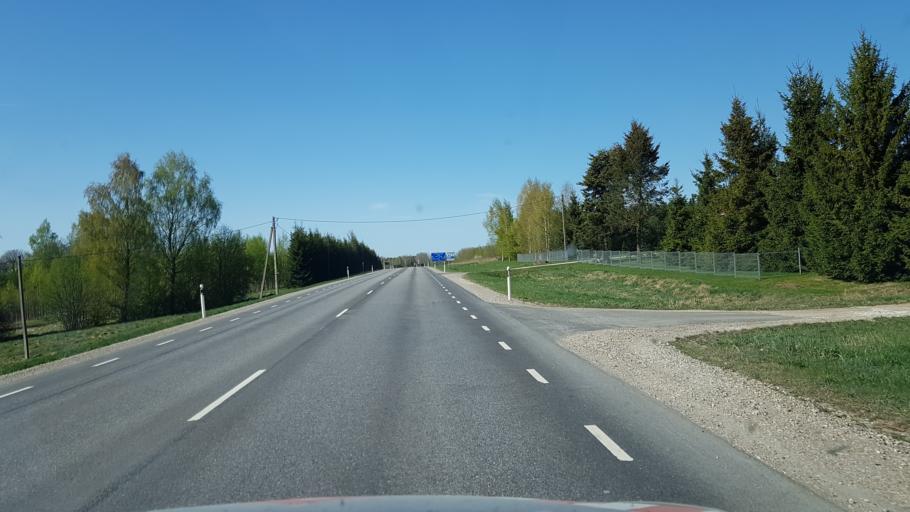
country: EE
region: Viljandimaa
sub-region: Viljandi linn
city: Viljandi
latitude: 58.3508
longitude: 25.5619
